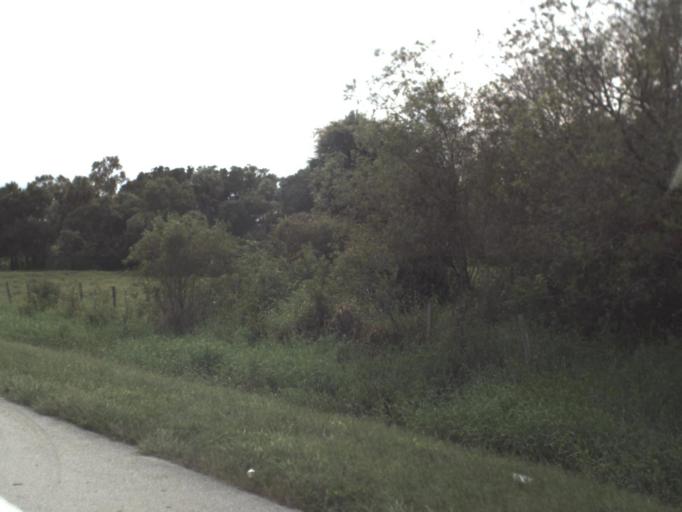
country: US
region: Florida
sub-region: Lee County
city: Fort Myers Shores
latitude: 26.7324
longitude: -81.7610
